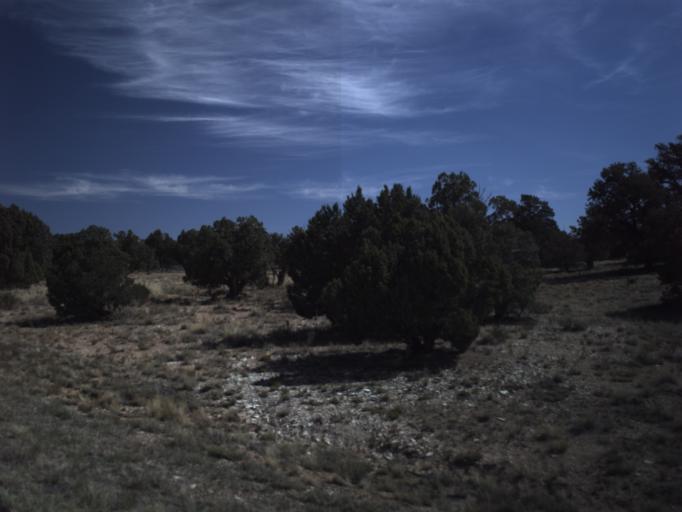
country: US
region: Utah
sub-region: Wayne County
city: Loa
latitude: 37.7280
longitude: -111.5218
